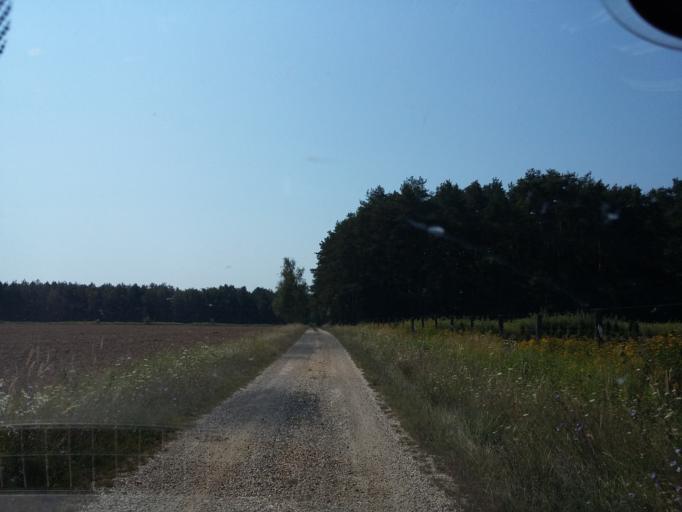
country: SI
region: Hodos-Hodos
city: Hodos
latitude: 46.8481
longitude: 16.3204
